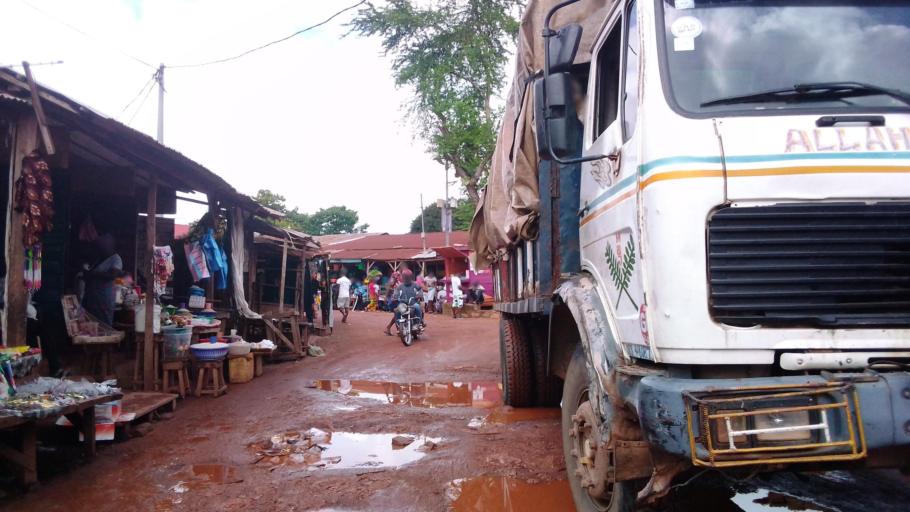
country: SL
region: Northern Province
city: Makeni
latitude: 8.8895
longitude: -12.0417
